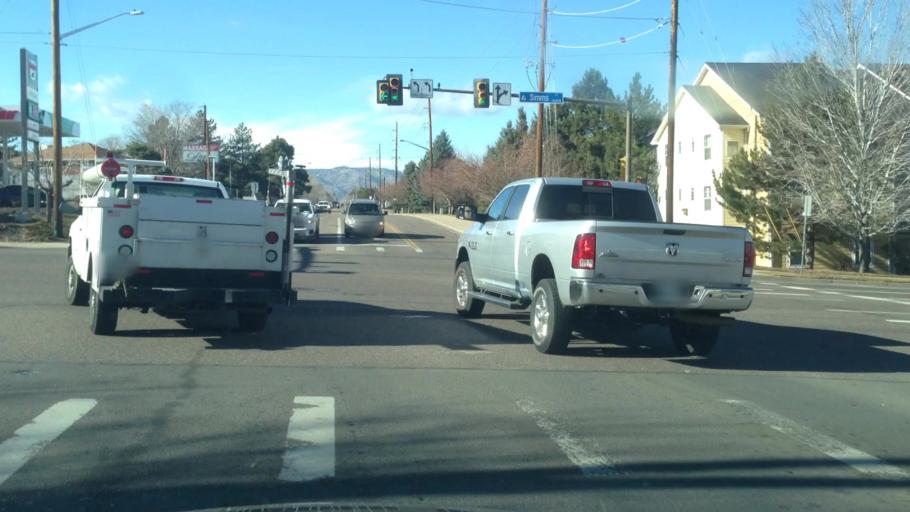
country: US
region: Colorado
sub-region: Jefferson County
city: Applewood
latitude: 39.7291
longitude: -105.1282
